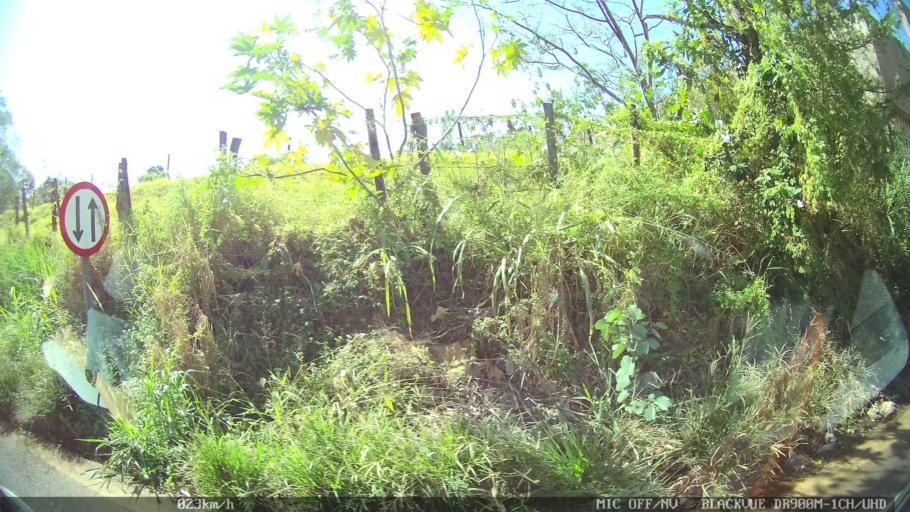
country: BR
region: Sao Paulo
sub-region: Batatais
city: Batatais
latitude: -20.8814
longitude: -47.6028
